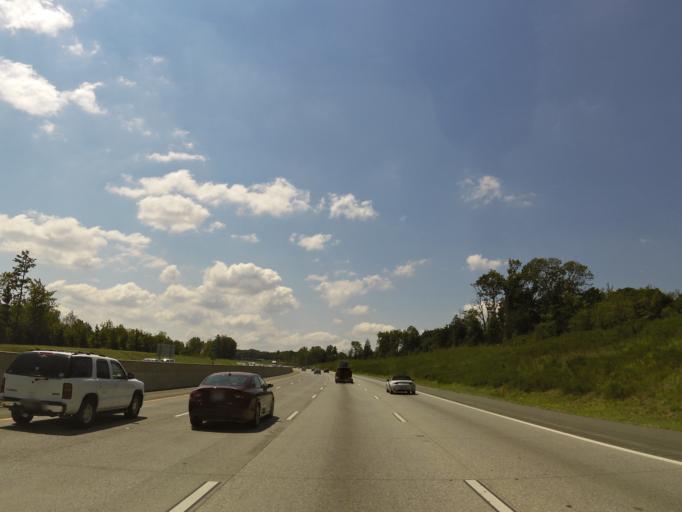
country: US
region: North Carolina
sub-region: Cabarrus County
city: Harrisburg
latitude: 35.4087
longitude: -80.6910
